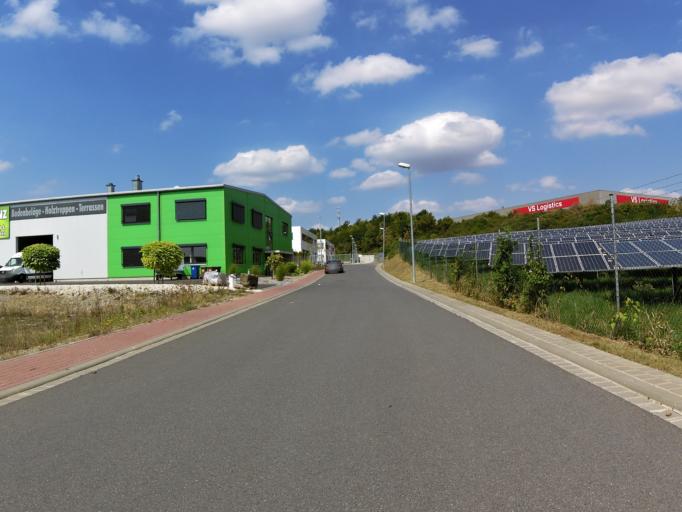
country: DE
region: Bavaria
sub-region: Regierungsbezirk Unterfranken
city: Estenfeld
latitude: 49.8421
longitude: 10.0127
